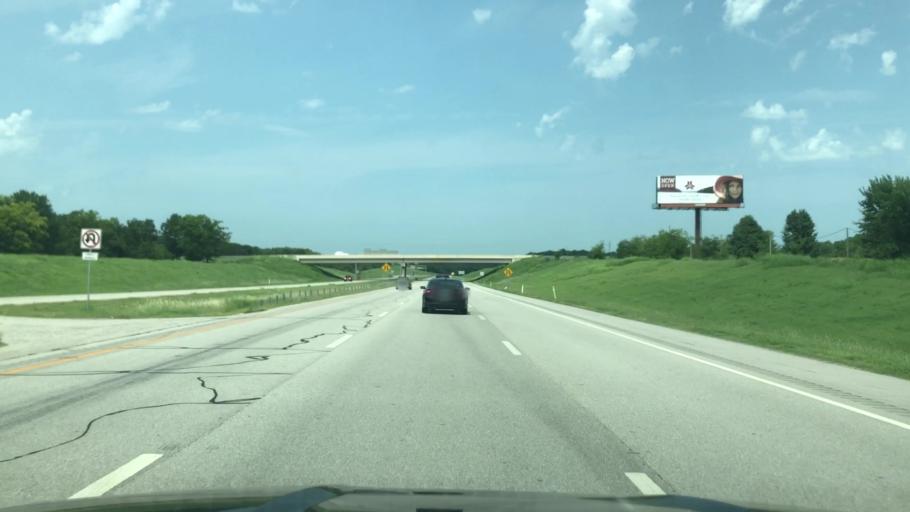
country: US
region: Oklahoma
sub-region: Rogers County
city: Catoosa
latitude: 36.1746
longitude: -95.7319
